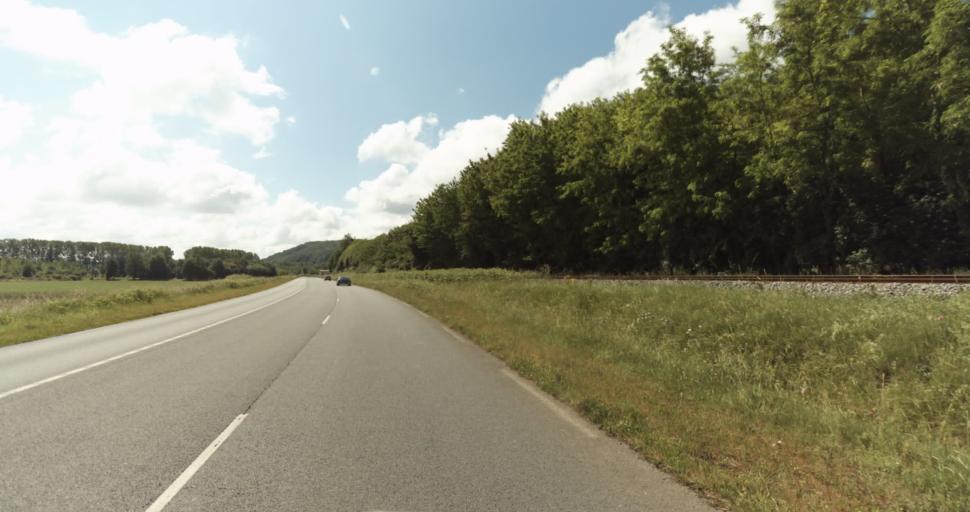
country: FR
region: Aquitaine
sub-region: Departement de la Dordogne
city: Belves
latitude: 44.8310
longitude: 0.9418
